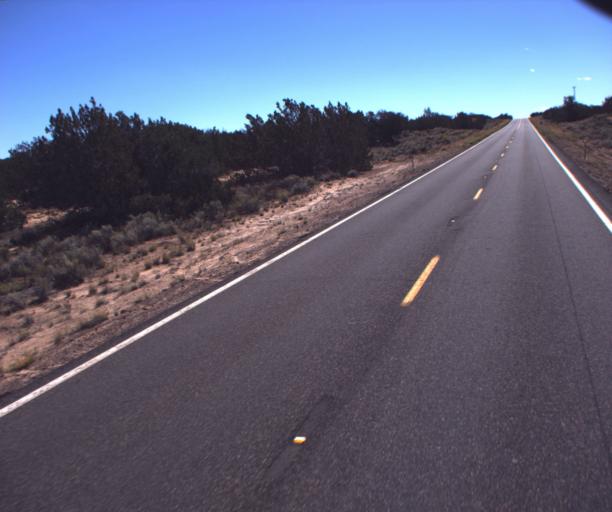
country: US
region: Arizona
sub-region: Apache County
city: Saint Johns
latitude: 34.8534
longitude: -109.2377
